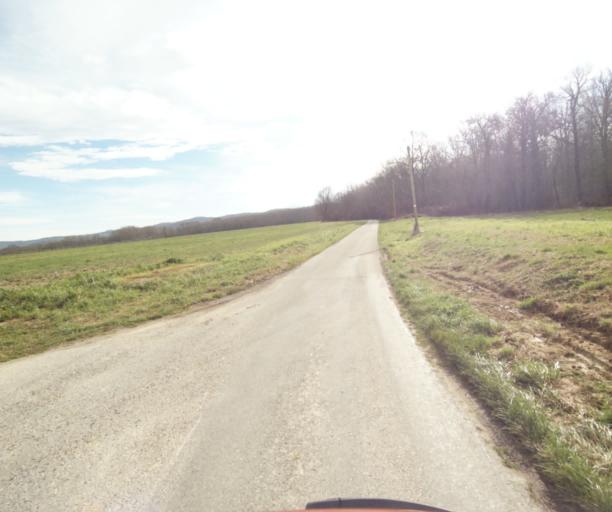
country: FR
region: Midi-Pyrenees
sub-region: Departement de l'Ariege
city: La Tour-du-Crieu
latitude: 43.0924
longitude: 1.7427
